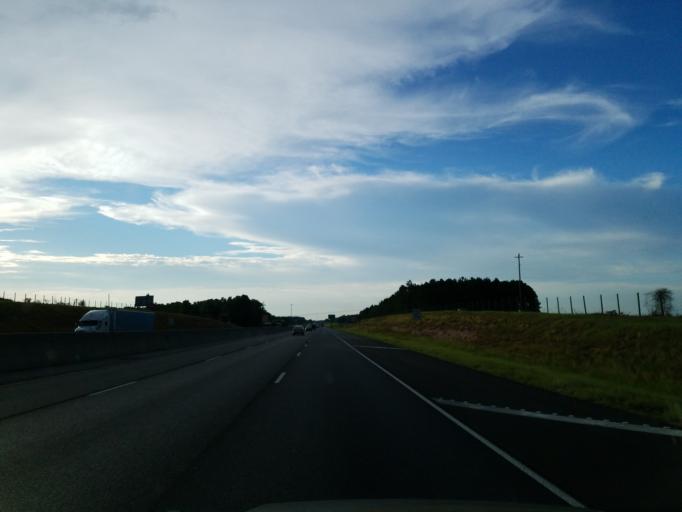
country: US
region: Georgia
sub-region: Tift County
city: Tifton
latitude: 31.5316
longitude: -83.5243
